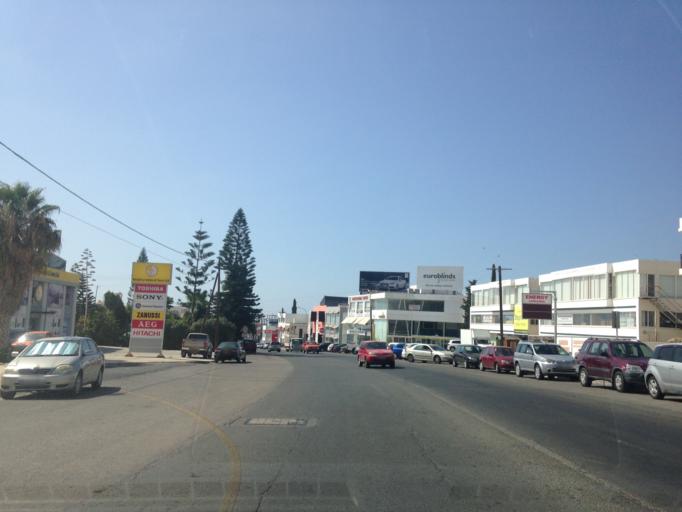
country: CY
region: Pafos
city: Empa
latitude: 34.7955
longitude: 32.4379
